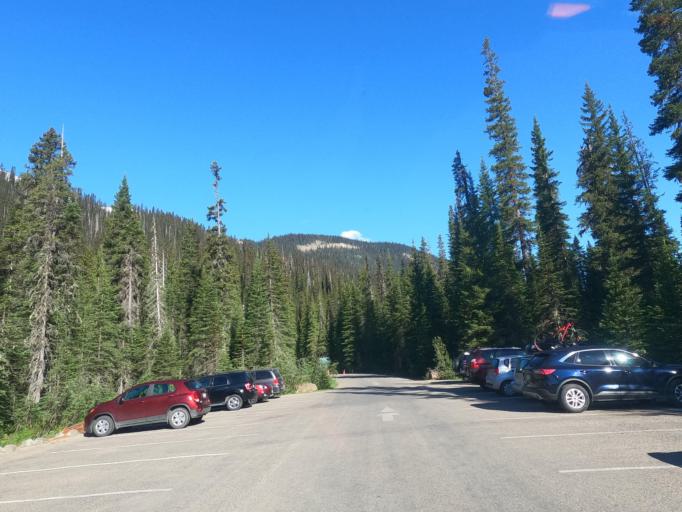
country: CA
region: Alberta
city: Lake Louise
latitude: 51.4982
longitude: -116.4838
